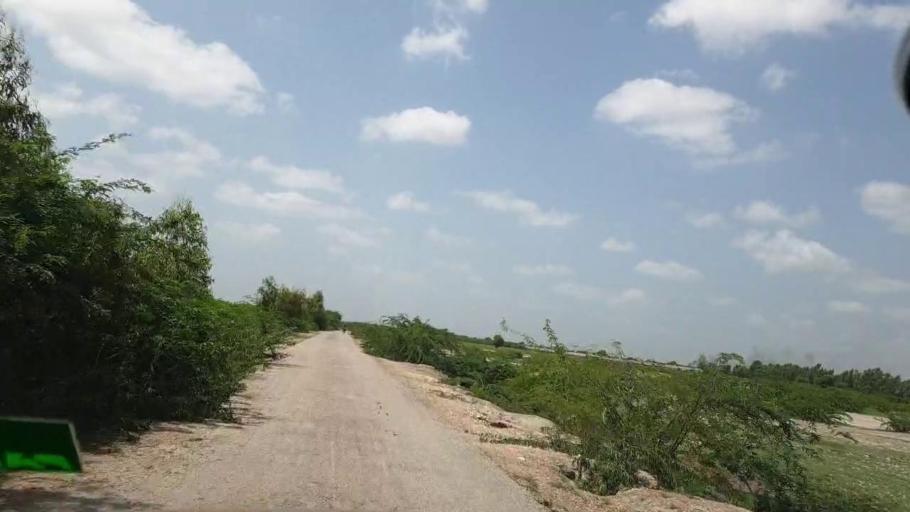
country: PK
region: Sindh
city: Kadhan
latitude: 24.5517
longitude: 69.2028
